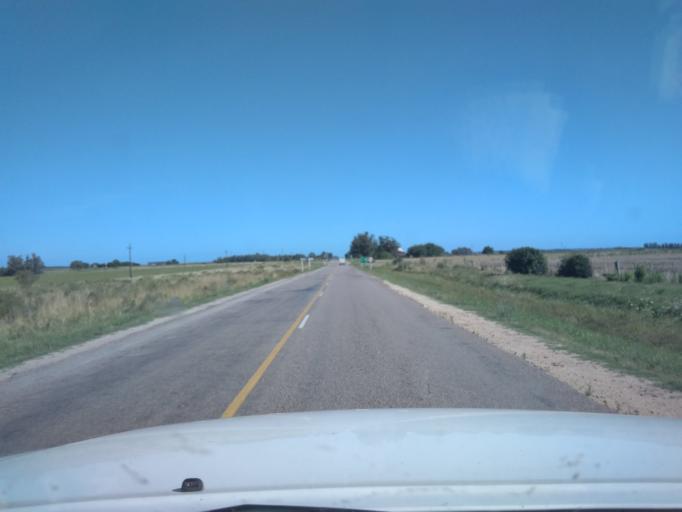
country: UY
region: Canelones
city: San Ramon
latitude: -34.2066
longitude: -55.9315
